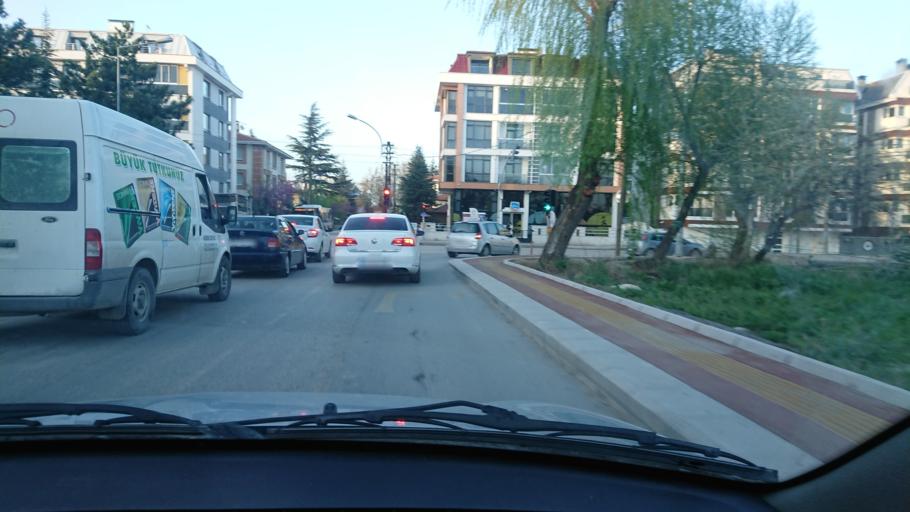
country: TR
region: Eskisehir
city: Eskisehir
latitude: 39.7700
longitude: 30.4782
